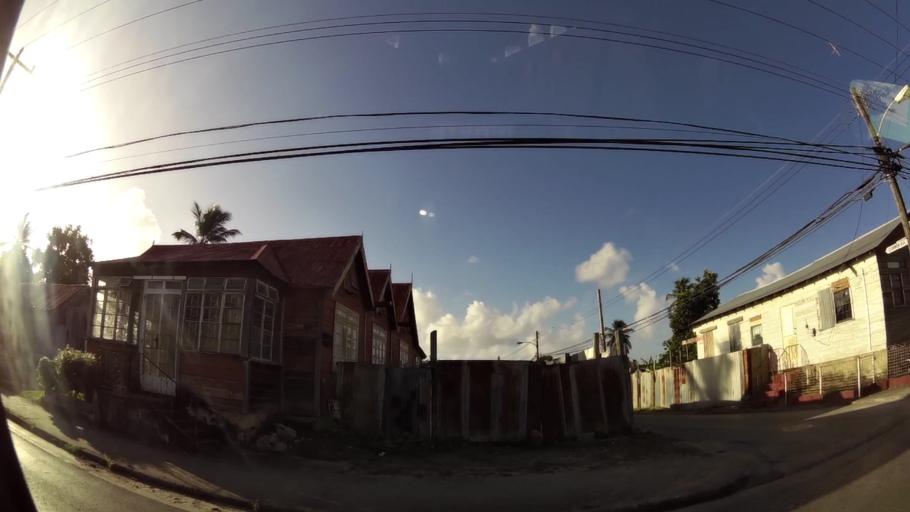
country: BB
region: Saint Michael
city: Bridgetown
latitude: 13.0878
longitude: -59.6047
